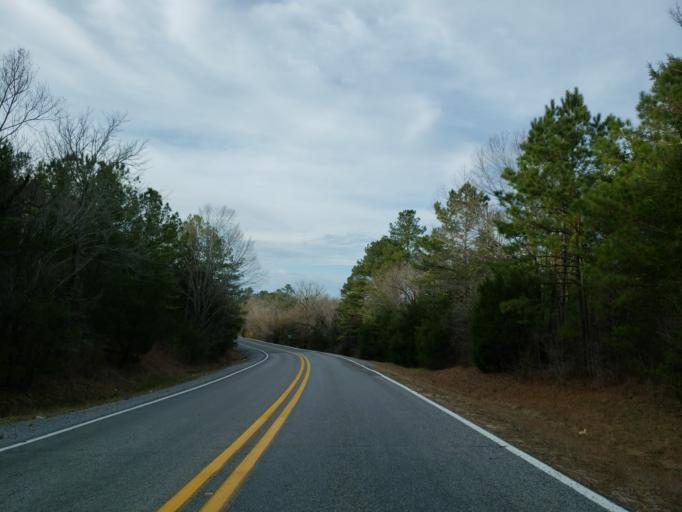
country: US
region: Mississippi
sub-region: Wayne County
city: Waynesboro
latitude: 31.8459
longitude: -88.6870
